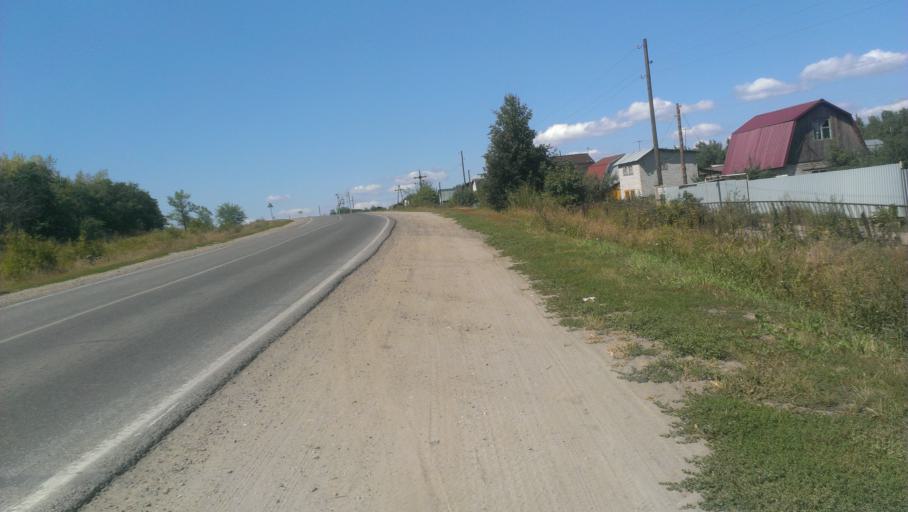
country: RU
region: Altai Krai
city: Gon'ba
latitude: 53.4177
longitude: 83.5487
